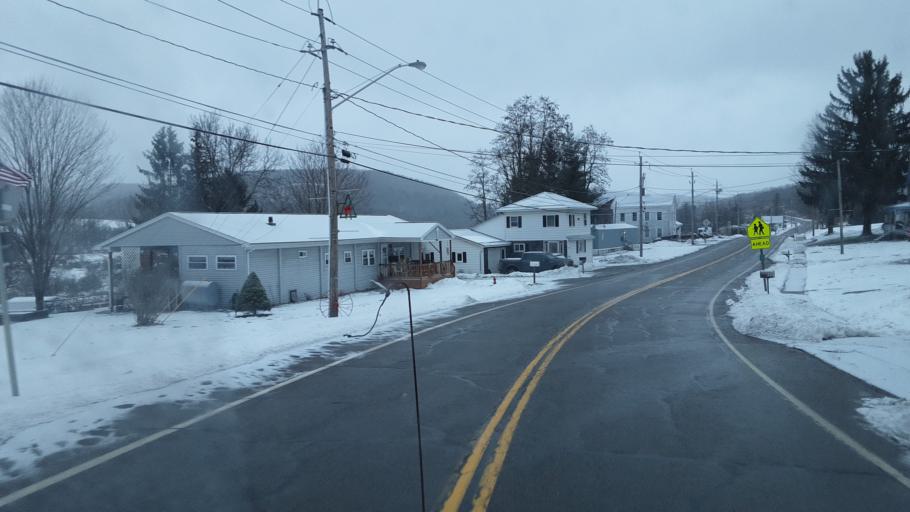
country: US
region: Pennsylvania
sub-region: Tioga County
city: Westfield
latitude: 42.0440
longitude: -77.5464
